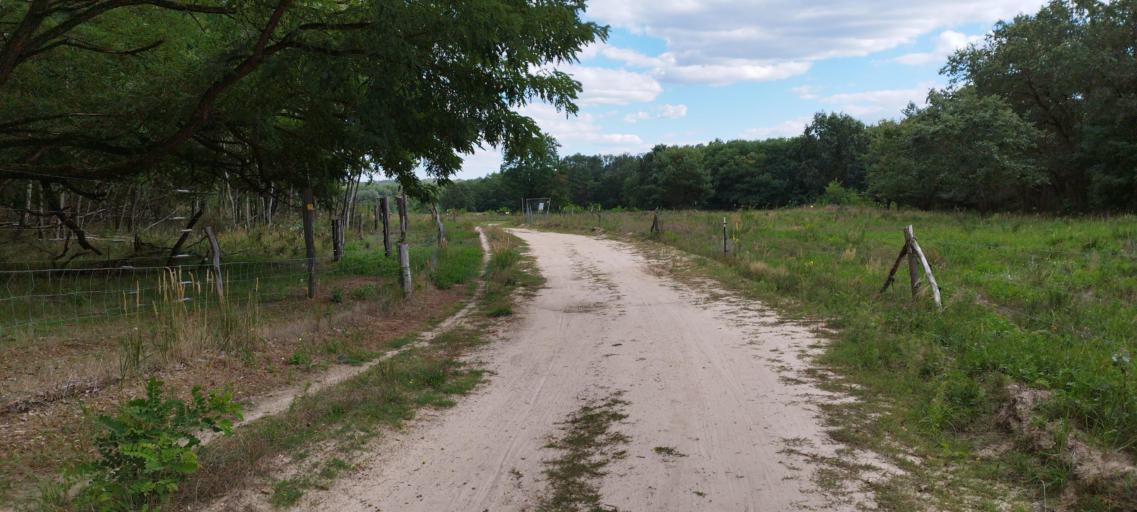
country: DE
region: Brandenburg
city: Dallgow-Doeberitz
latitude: 52.4821
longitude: 13.0309
